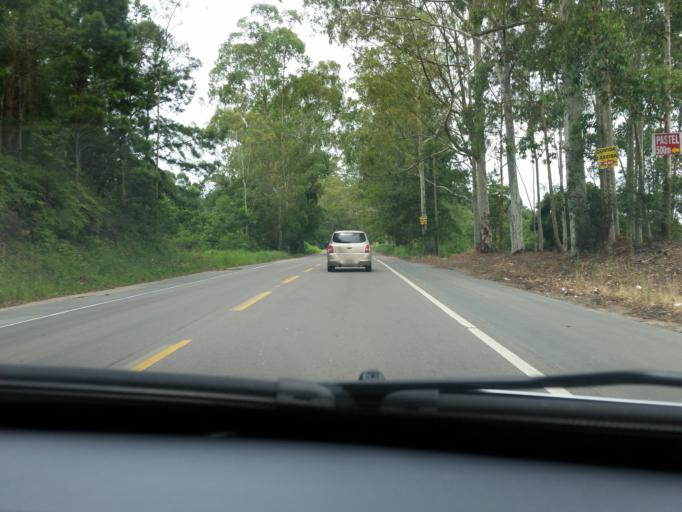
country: BR
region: Santa Catarina
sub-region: Rio Do Sul
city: Rio do Sul
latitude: -27.1707
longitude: -49.5763
